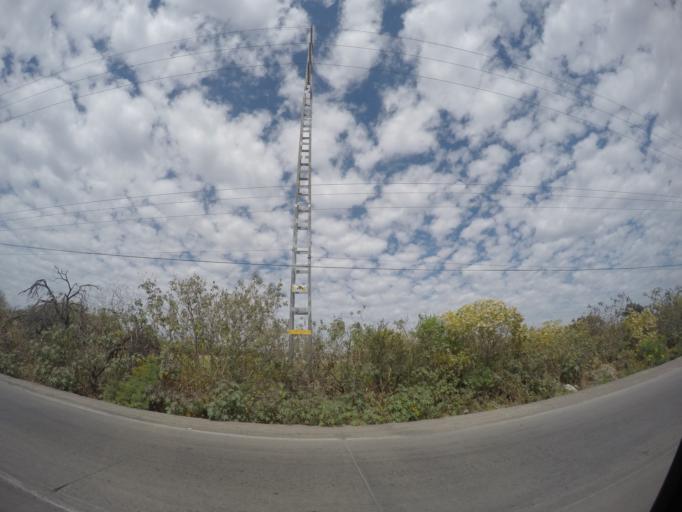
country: MX
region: Guanajuato
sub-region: Leon
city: San Antonio de los Tepetates
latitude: 21.0505
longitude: -101.6893
